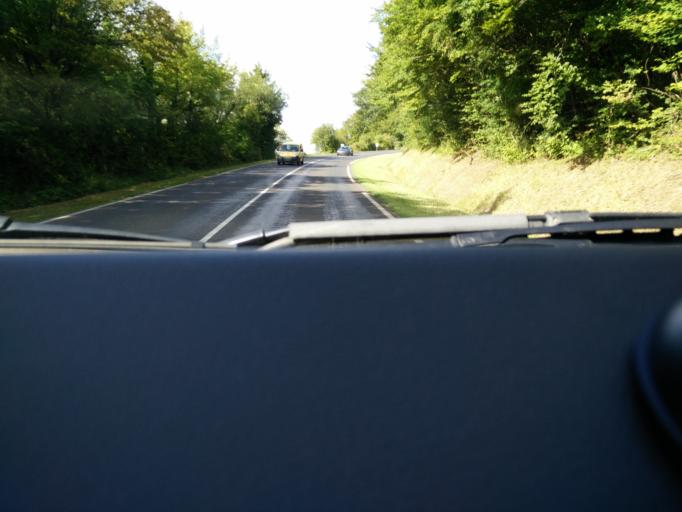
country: FR
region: Lorraine
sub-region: Departement de la Meuse
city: Etain
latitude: 49.1185
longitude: 5.5557
